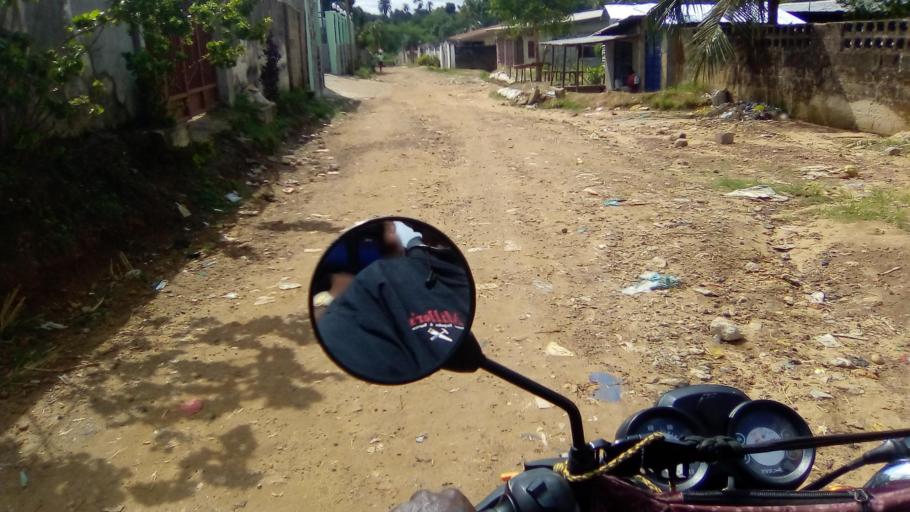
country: SL
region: Southern Province
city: Bo
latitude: 7.9561
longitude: -11.7468
